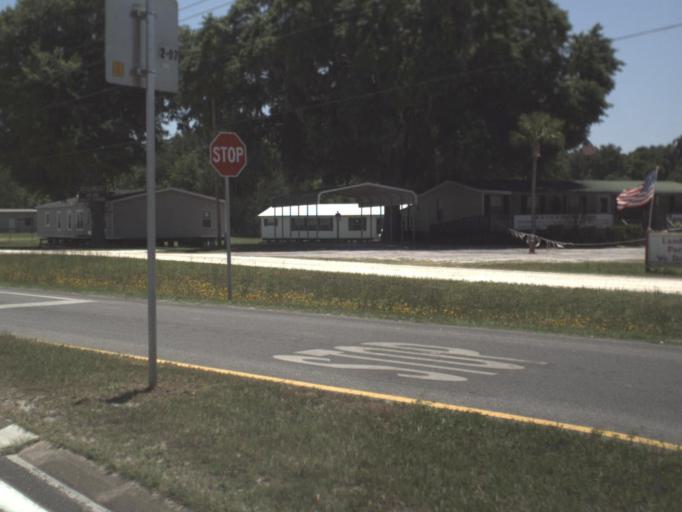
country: US
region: Florida
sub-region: Suwannee County
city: Live Oak
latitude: 30.2857
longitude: -82.9590
